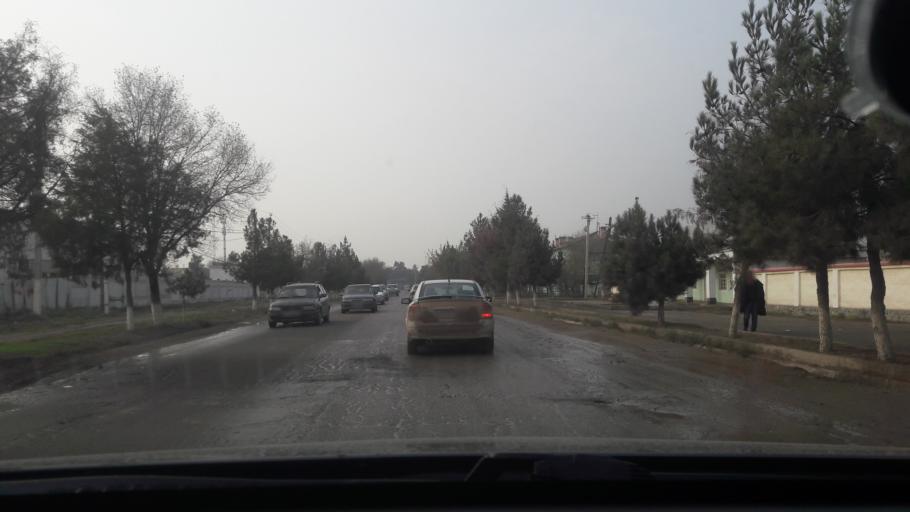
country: TJ
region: Khatlon
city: Abdurahmoni Jomi
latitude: 37.9830
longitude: 68.6980
